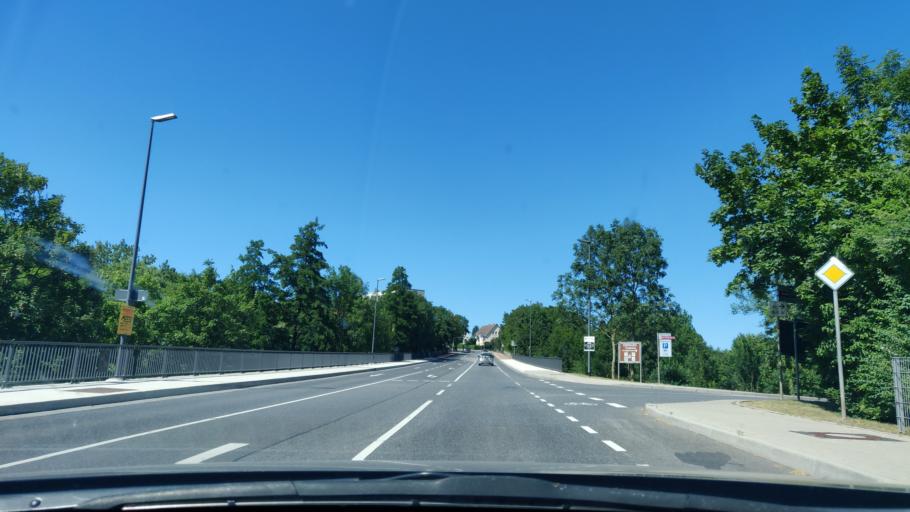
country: DE
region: Hesse
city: Fritzlar
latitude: 51.1283
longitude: 9.2808
